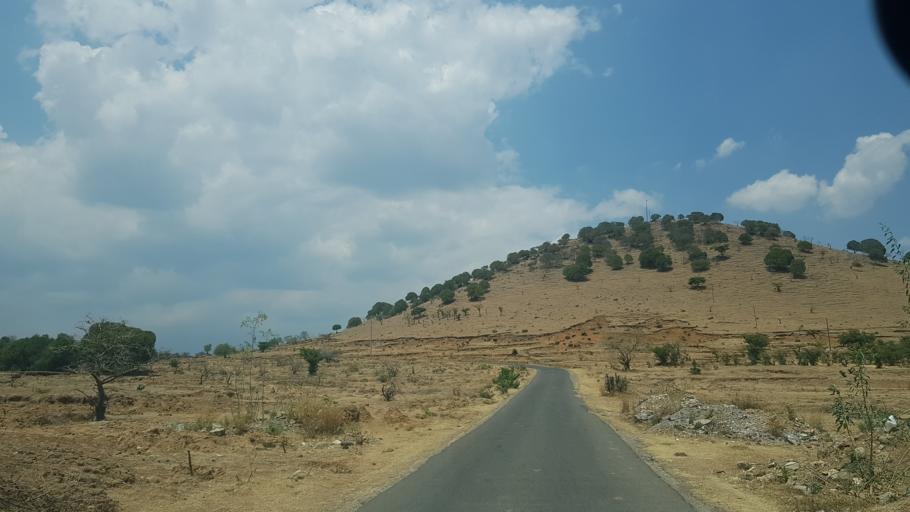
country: MX
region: Puebla
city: San Juan Amecac
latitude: 18.8118
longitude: -98.6244
